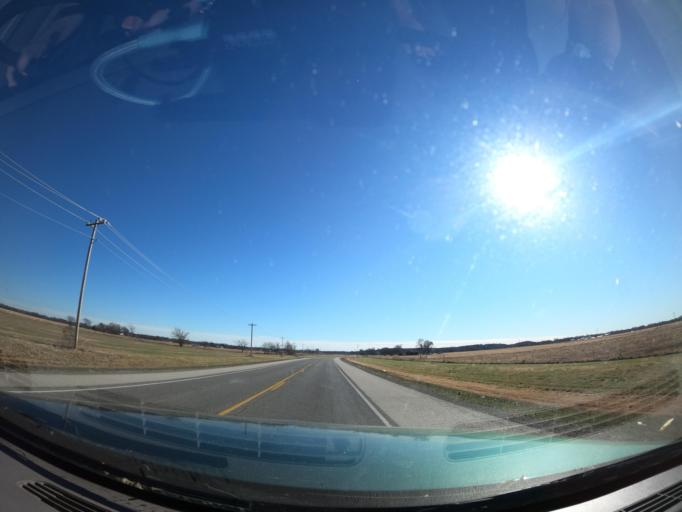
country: US
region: Oklahoma
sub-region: Muskogee County
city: Haskell
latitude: 35.7979
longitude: -95.6697
